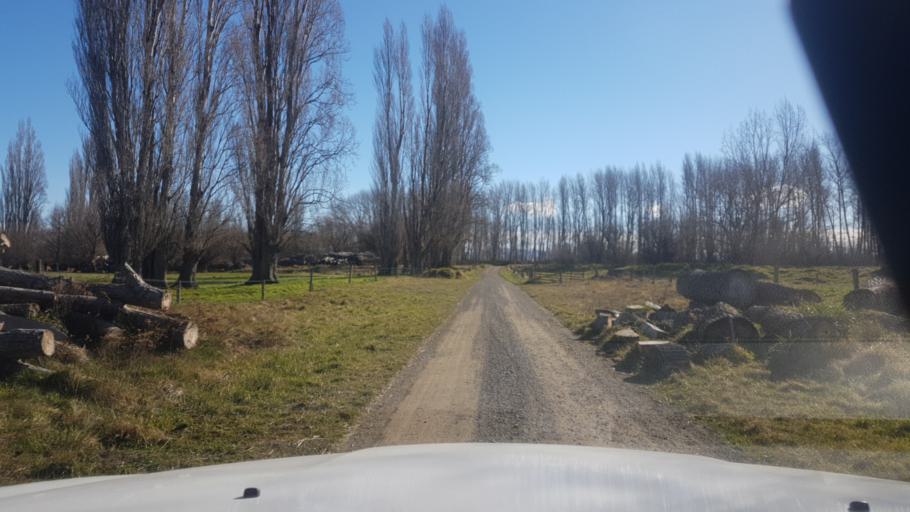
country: NZ
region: Canterbury
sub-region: Timaru District
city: Pleasant Point
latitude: -44.2501
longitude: 171.1081
